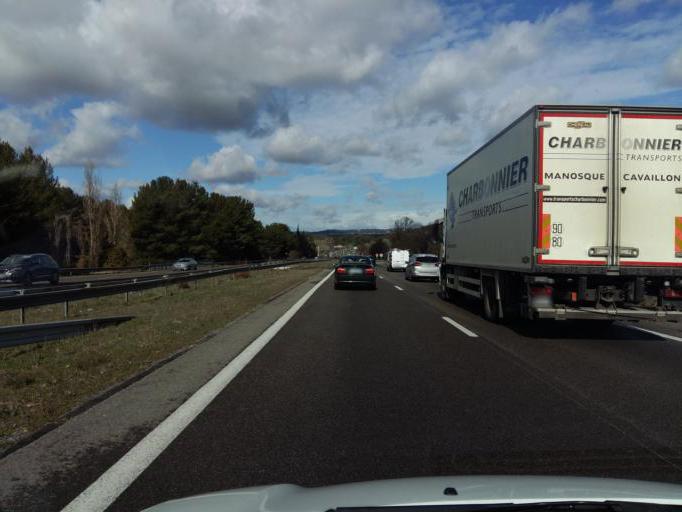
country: FR
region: Provence-Alpes-Cote d'Azur
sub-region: Departement des Bouches-du-Rhone
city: Bouc-Bel-Air
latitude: 43.4892
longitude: 5.4076
